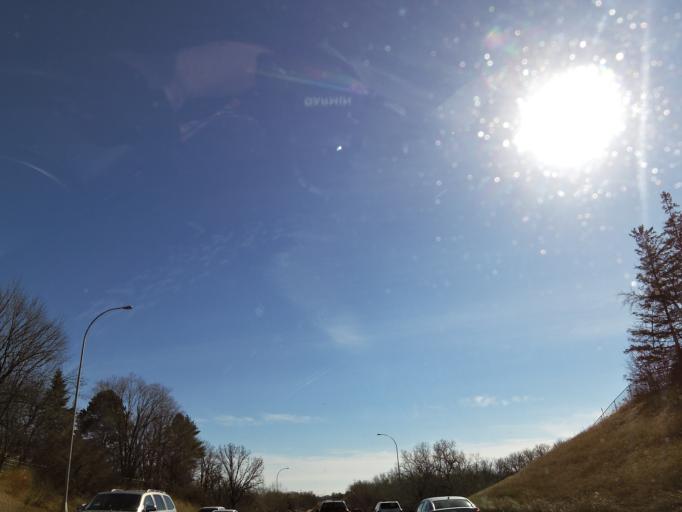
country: US
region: Minnesota
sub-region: Hennepin County
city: Minnetonka Mills
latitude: 44.9646
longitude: -93.4008
